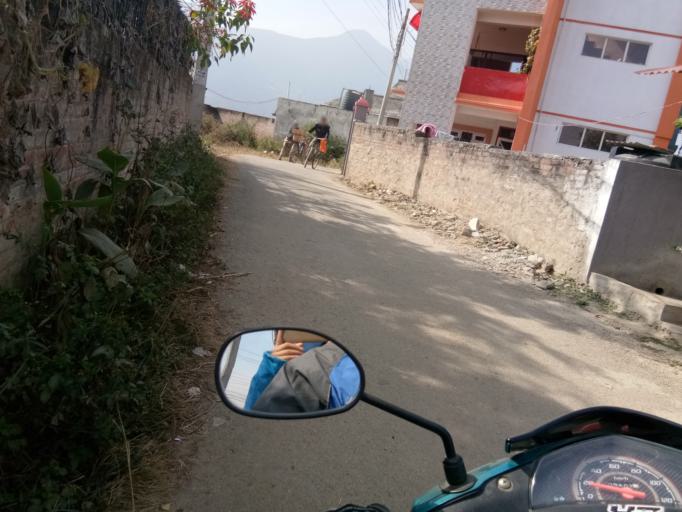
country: NP
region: Central Region
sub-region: Bagmati Zone
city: Patan
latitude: 27.6521
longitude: 85.2983
